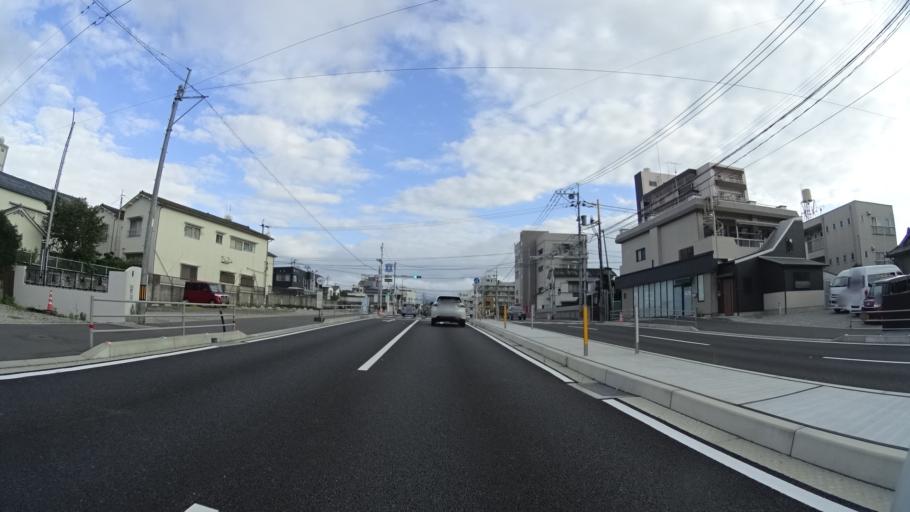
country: JP
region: Oita
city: Beppu
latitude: 33.2828
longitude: 131.4969
